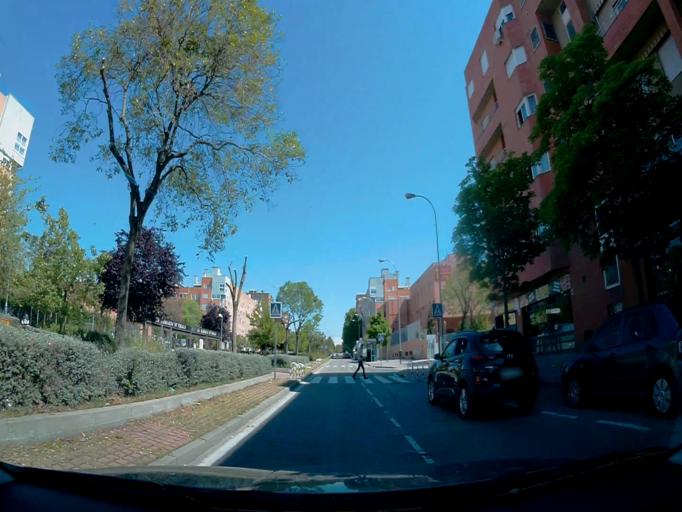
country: ES
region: Madrid
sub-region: Provincia de Madrid
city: Vicalvaro
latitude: 40.4012
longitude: -3.6209
